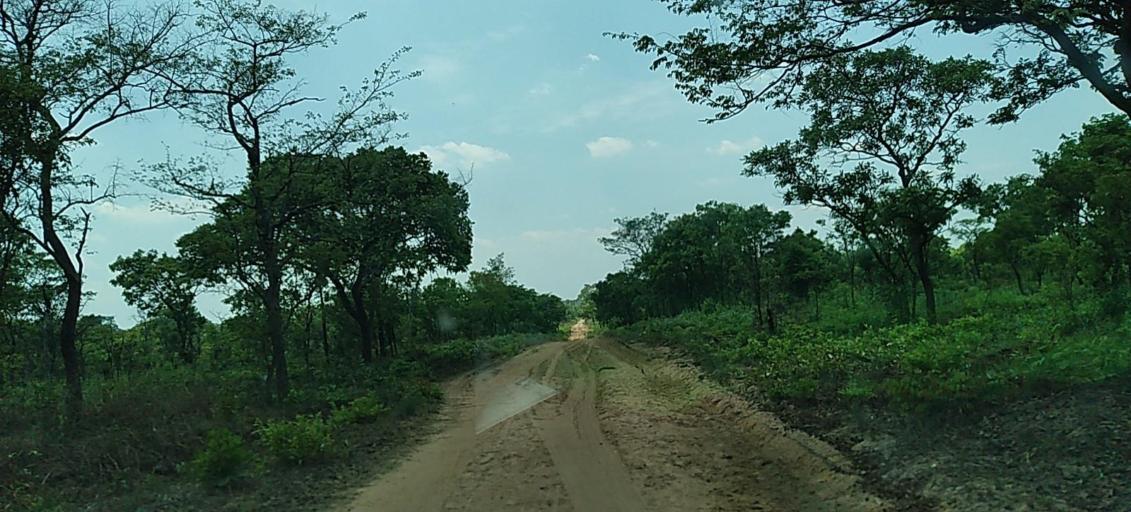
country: CD
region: Katanga
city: Kolwezi
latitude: -11.3483
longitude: 25.2150
